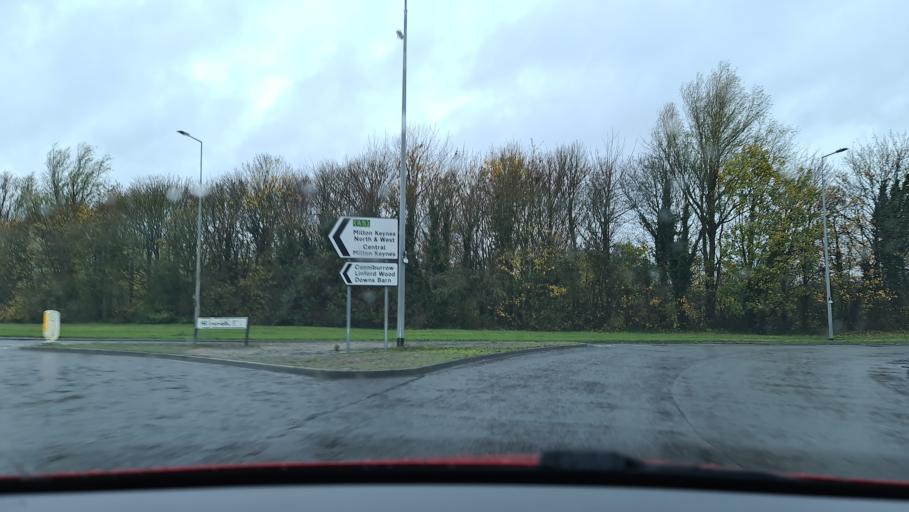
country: GB
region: England
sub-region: Milton Keynes
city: Milton Keynes
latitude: 52.0583
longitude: -0.7449
